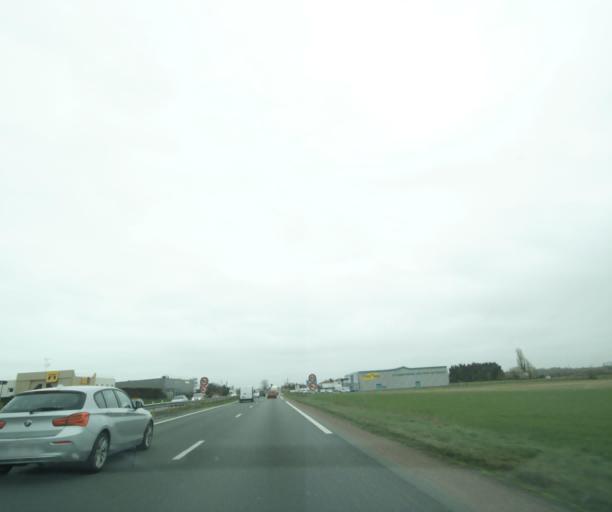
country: FR
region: Poitou-Charentes
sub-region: Departement de la Charente-Maritime
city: Angoulins
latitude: 46.1078
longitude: -1.0986
